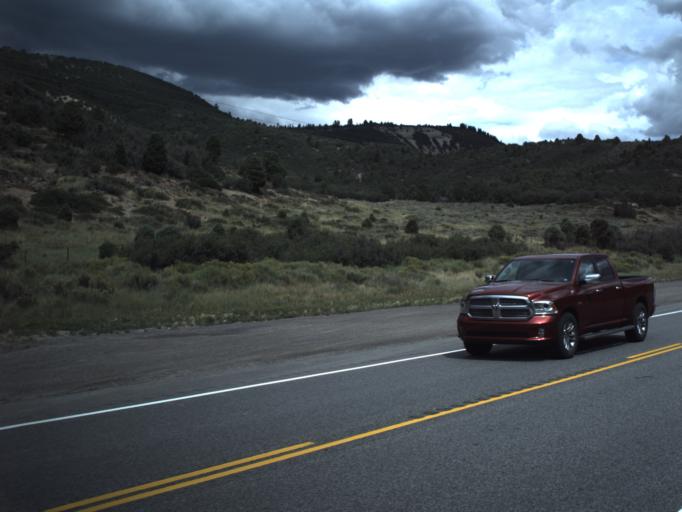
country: US
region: Utah
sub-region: Carbon County
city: Helper
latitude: 39.9341
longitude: -111.1152
